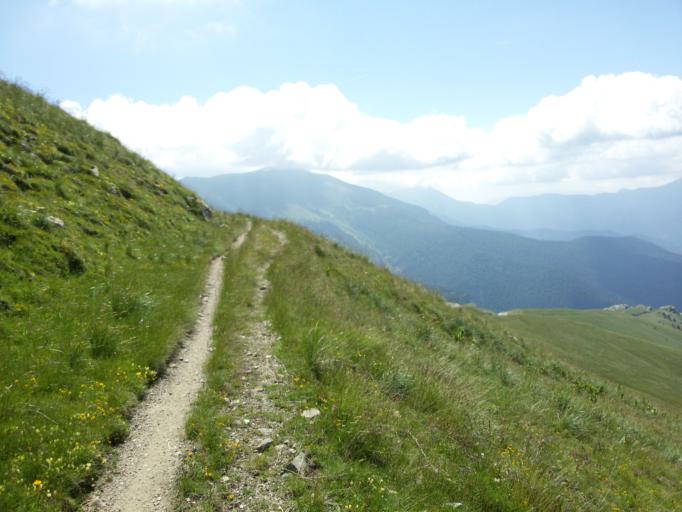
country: IT
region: Piedmont
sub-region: Provincia di Cuneo
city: Limone Piemonte
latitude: 44.1478
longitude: 7.6194
